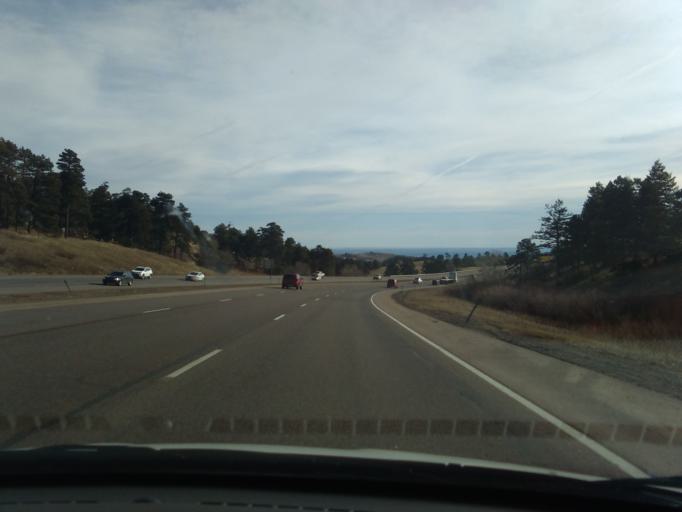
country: US
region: Colorado
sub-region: Jefferson County
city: Genesee
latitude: 39.7089
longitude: -105.2849
